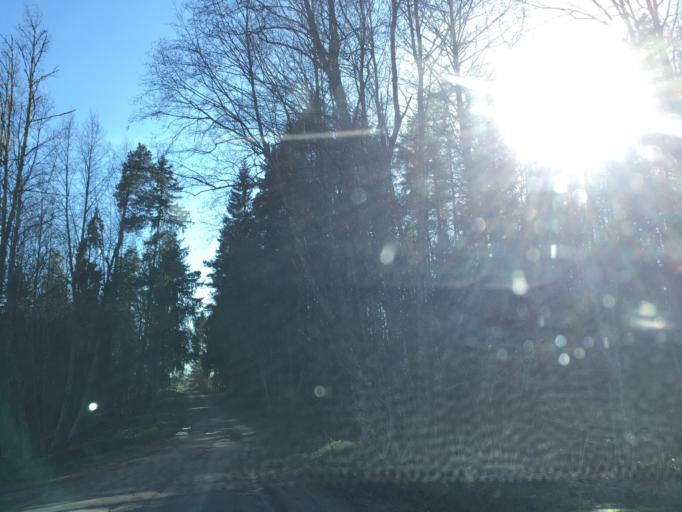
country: EE
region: Valgamaa
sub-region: Valga linn
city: Valga
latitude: 57.7702
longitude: 26.2178
